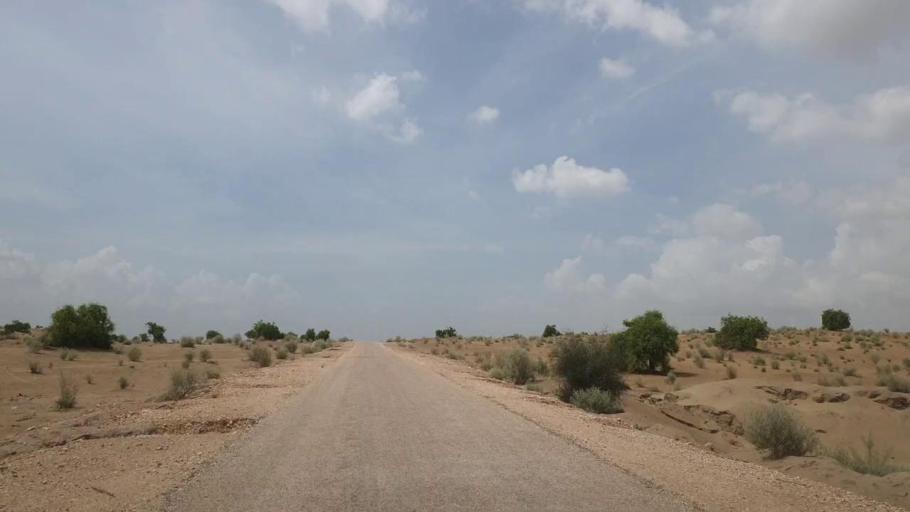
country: PK
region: Sindh
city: Kot Diji
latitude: 27.2041
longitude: 69.0860
